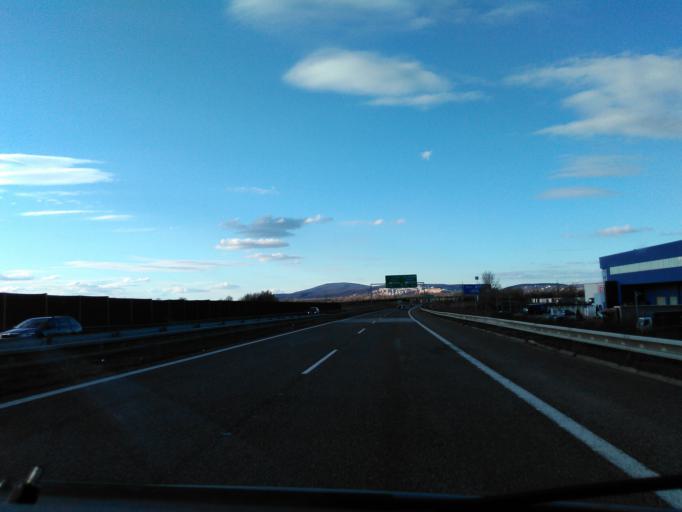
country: AT
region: Burgenland
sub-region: Politischer Bezirk Neusiedl am See
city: Kittsee
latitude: 48.1099
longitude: 17.0856
